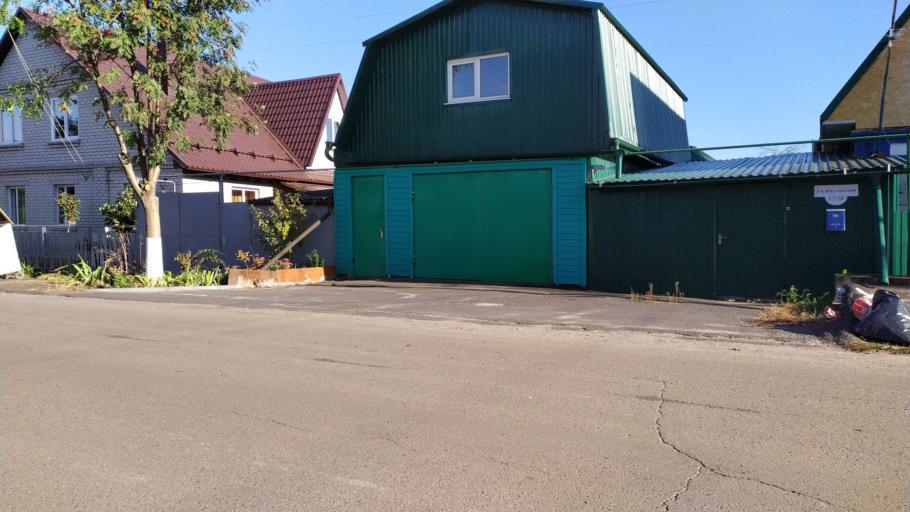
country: RU
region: Kursk
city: Kursk
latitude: 51.6430
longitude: 36.1421
